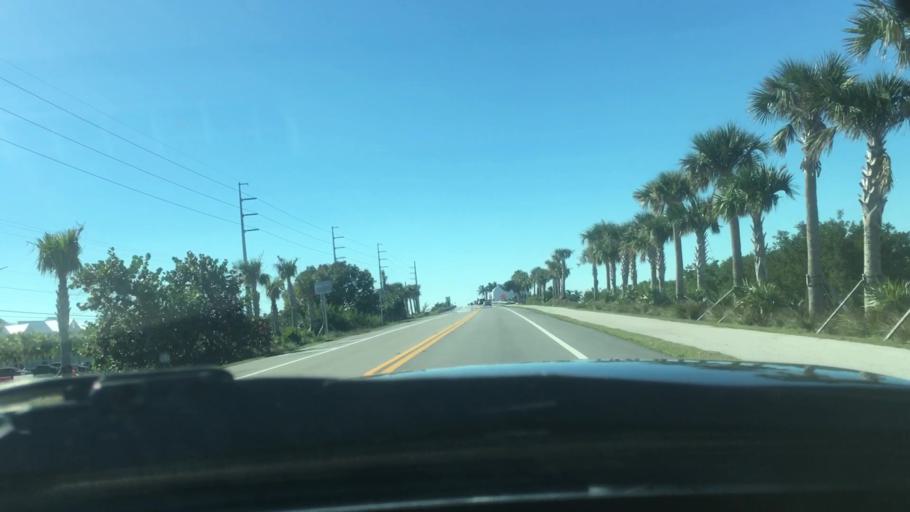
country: US
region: Florida
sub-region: Monroe County
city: Marathon
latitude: 24.7075
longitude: -81.1201
